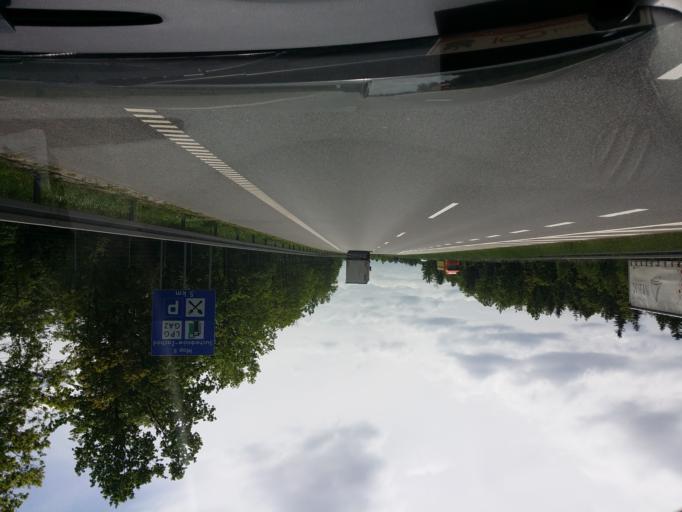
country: PL
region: Swietokrzyskie
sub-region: Powiat skarzyski
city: Suchedniow
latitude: 51.0773
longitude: 20.8363
